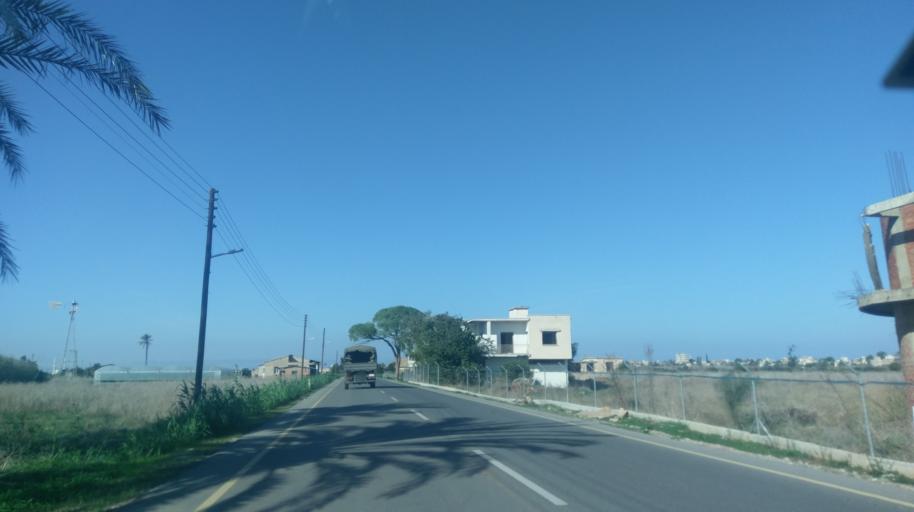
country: CY
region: Ammochostos
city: Deryneia
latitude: 35.0879
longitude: 33.9544
